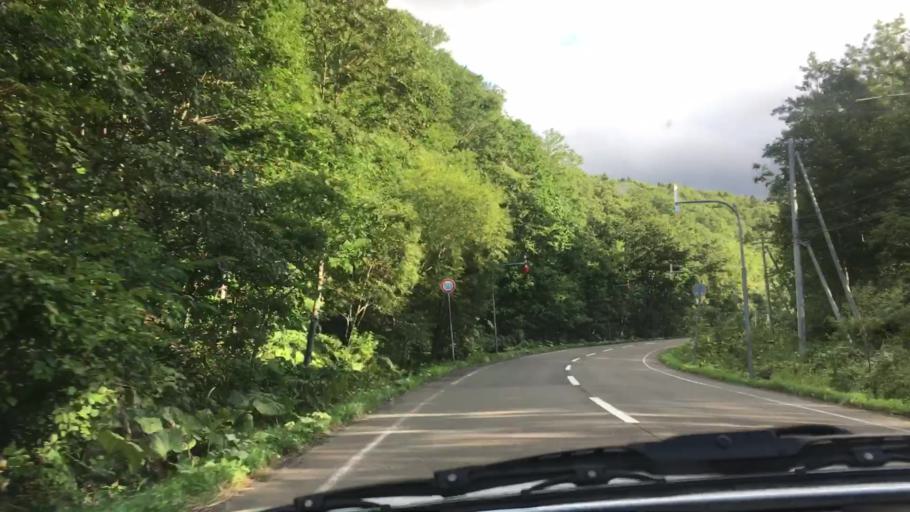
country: JP
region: Hokkaido
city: Shimo-furano
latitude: 43.0974
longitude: 142.6858
